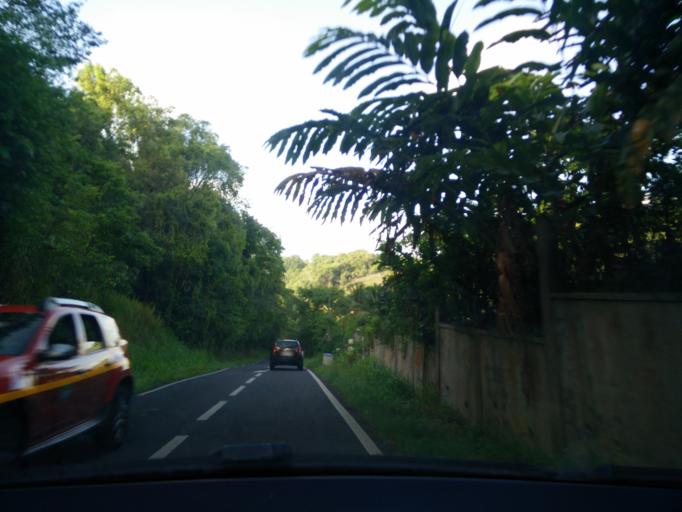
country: GP
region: Guadeloupe
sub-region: Guadeloupe
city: Sainte-Anne
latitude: 16.2796
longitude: -61.4173
